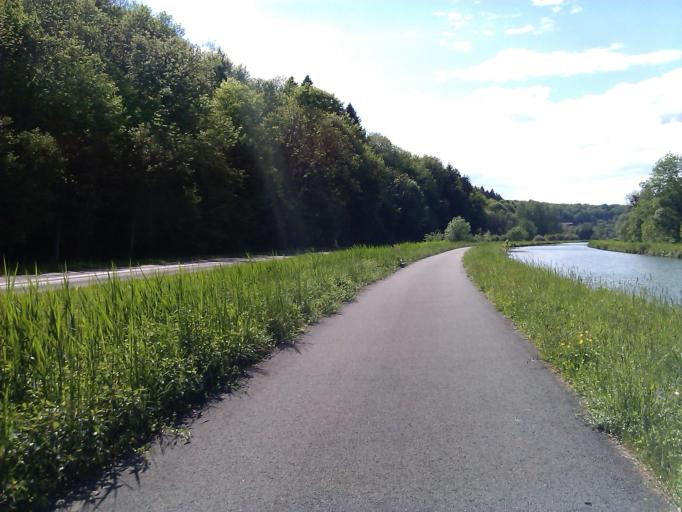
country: FR
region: Franche-Comte
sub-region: Departement du Doubs
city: Colombier-Fontaine
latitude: 47.4264
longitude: 6.6202
